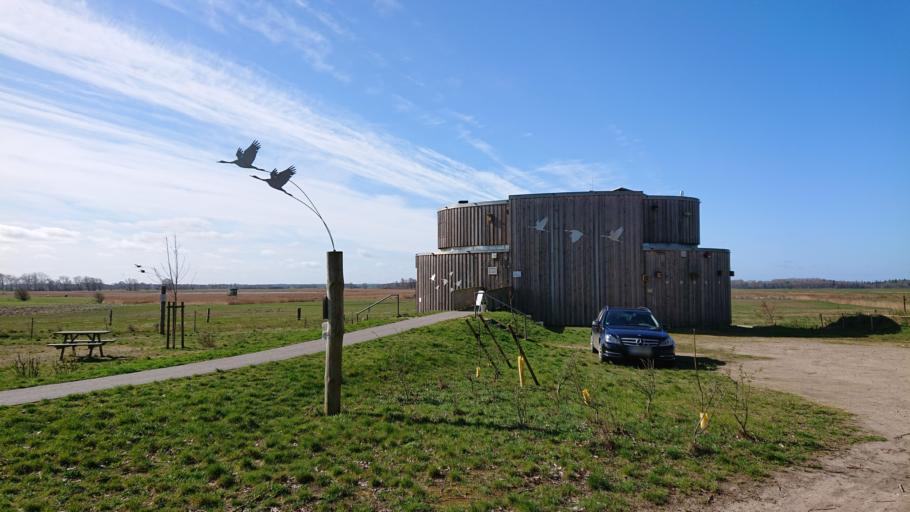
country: DE
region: Mecklenburg-Vorpommern
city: Altenpleen
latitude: 54.3658
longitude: 12.9043
